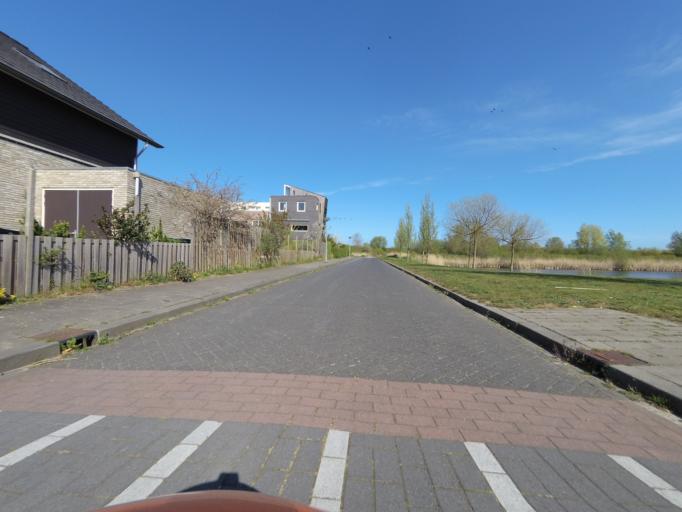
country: NL
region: Flevoland
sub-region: Gemeente Almere
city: Almere Stad
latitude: 52.4007
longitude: 5.1732
